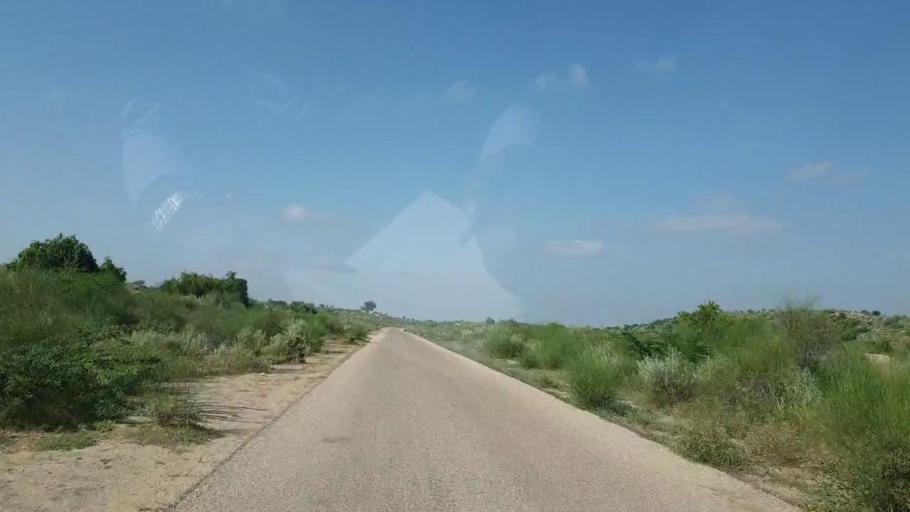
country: PK
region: Sindh
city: Mithi
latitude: 24.5628
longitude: 69.9086
